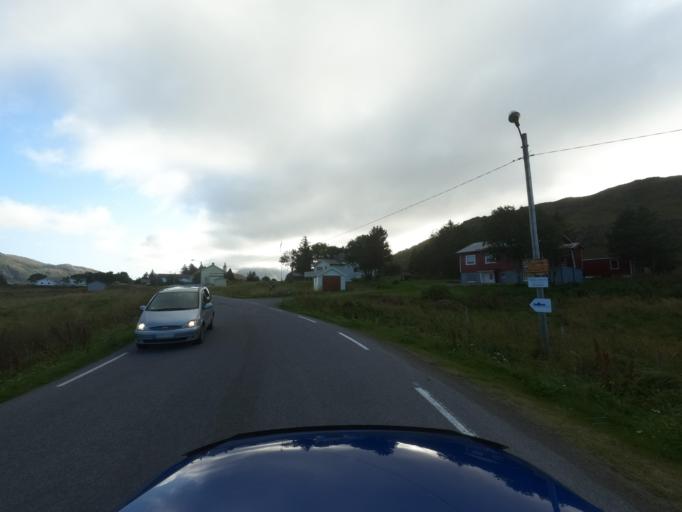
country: NO
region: Nordland
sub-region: Flakstad
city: Ramberg
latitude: 68.0877
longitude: 13.1661
